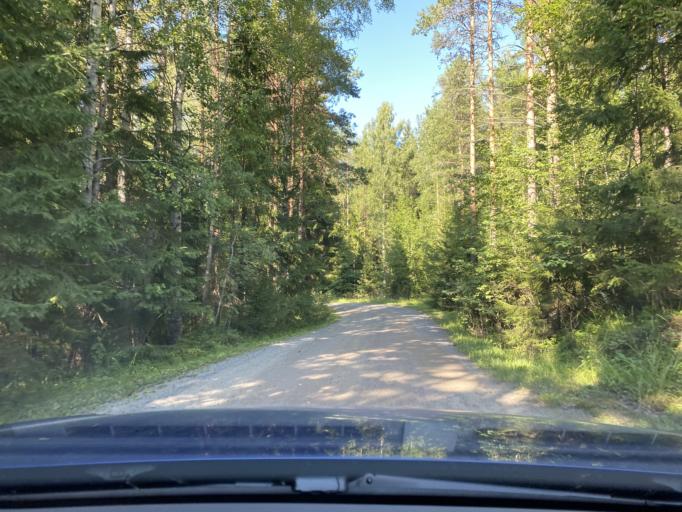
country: FI
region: Satakunta
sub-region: Rauma
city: Kiukainen
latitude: 61.1397
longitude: 22.0253
